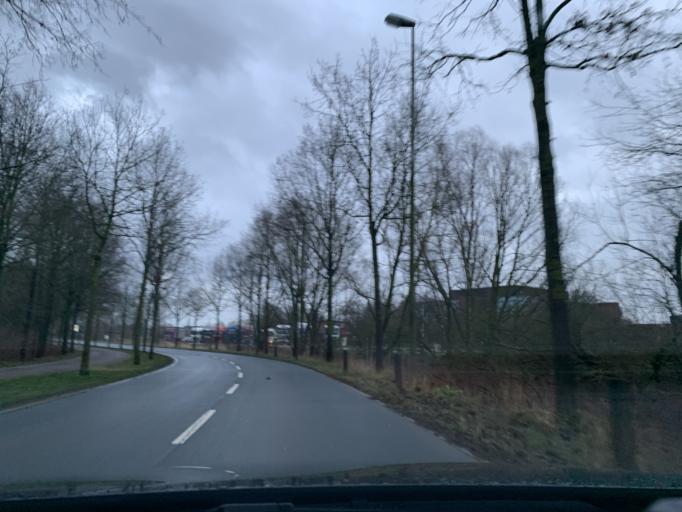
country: DE
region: Lower Saxony
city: Ritterhude
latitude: 53.1410
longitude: 8.7105
